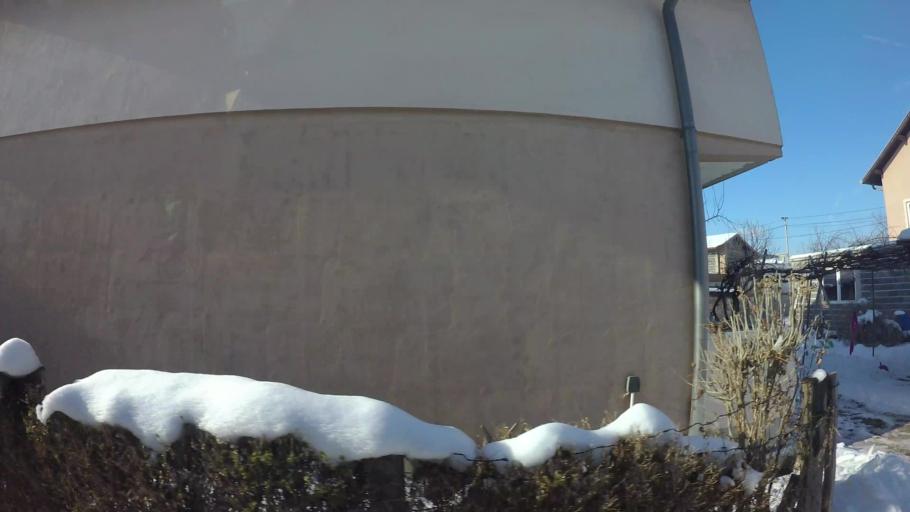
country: BA
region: Federation of Bosnia and Herzegovina
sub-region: Kanton Sarajevo
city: Sarajevo
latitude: 43.8088
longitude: 18.3294
